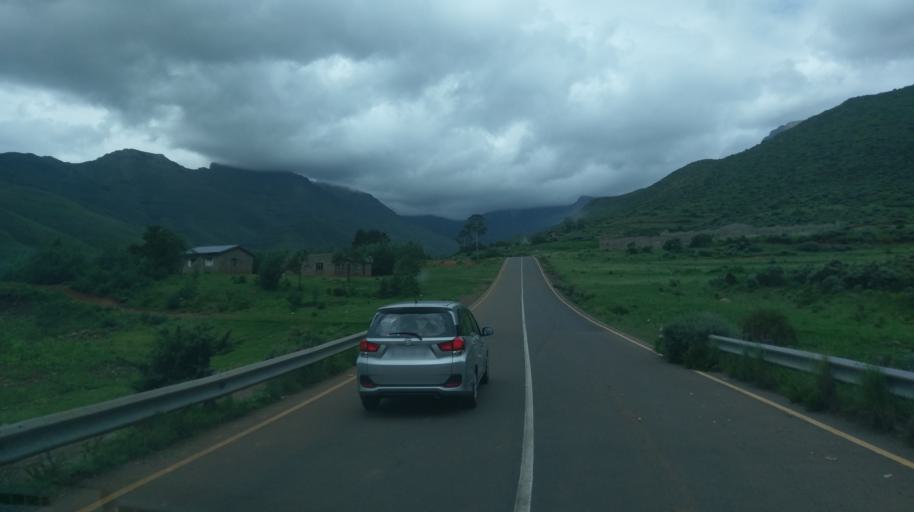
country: LS
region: Butha-Buthe
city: Butha-Buthe
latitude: -29.0499
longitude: 28.3298
